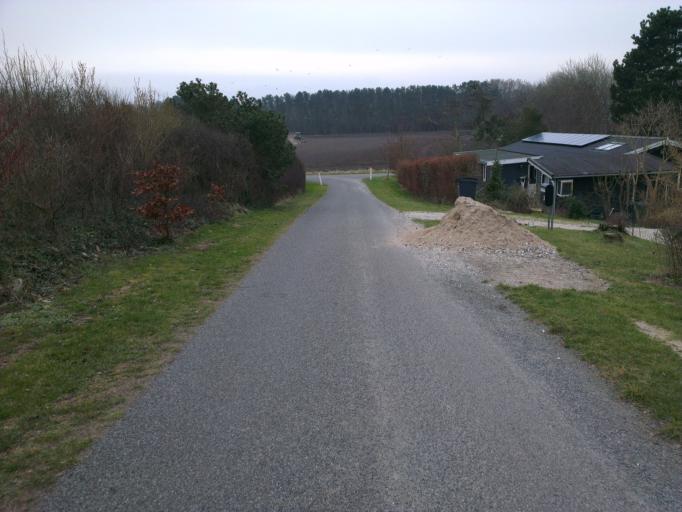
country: DK
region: Capital Region
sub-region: Frederikssund Kommune
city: Jaegerspris
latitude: 55.8288
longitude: 11.9545
